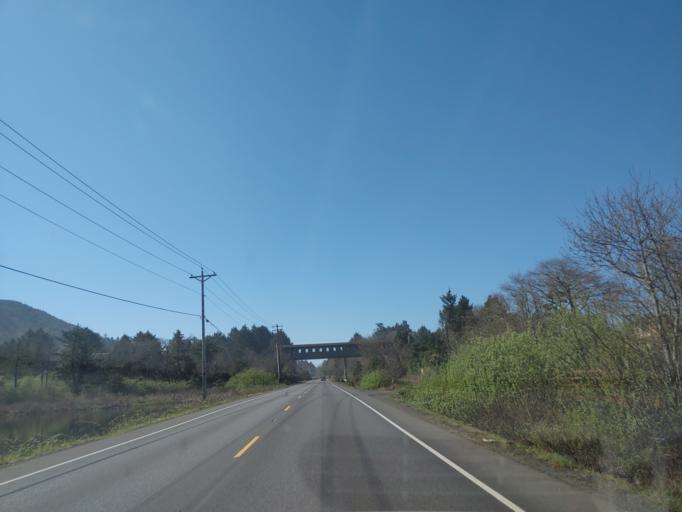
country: US
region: Oregon
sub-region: Tillamook County
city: Rockaway Beach
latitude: 45.5937
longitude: -123.9472
